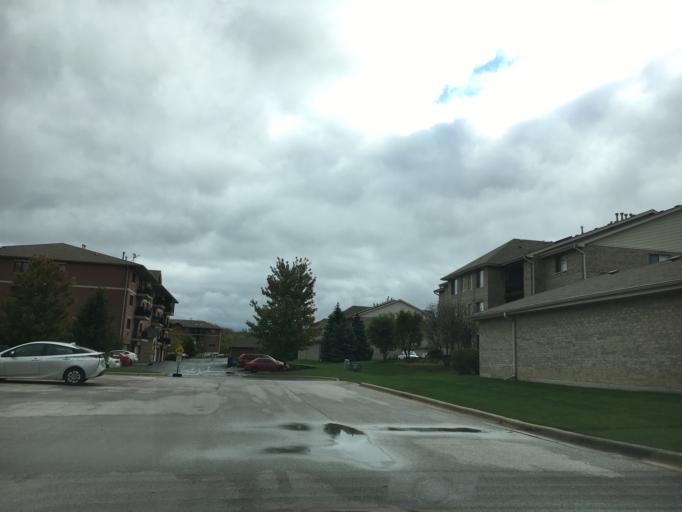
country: US
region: Illinois
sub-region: Cook County
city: Tinley Park
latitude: 41.6161
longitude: -87.7891
